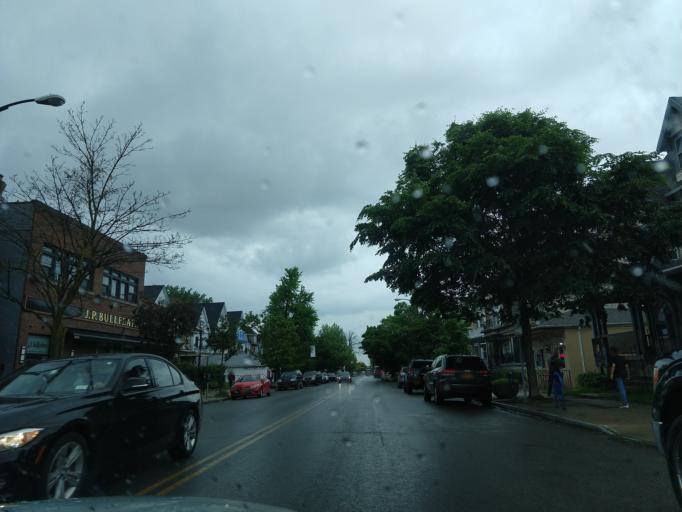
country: US
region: New York
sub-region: Erie County
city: Buffalo
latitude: 42.9245
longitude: -78.8771
